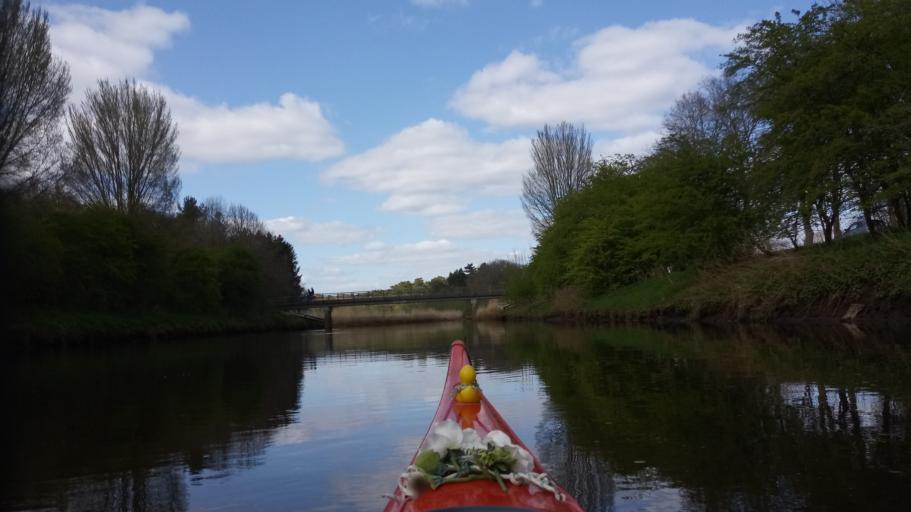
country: NL
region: Overijssel
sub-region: Gemeente Twenterand
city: Den Ham
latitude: 52.4706
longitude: 6.4536
